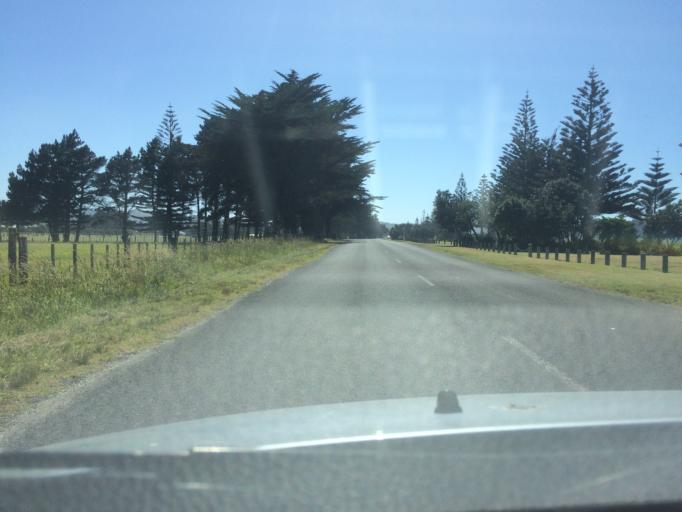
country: NZ
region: Gisborne
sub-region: Gisborne District
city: Gisborne
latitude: -38.6733
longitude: 177.9913
